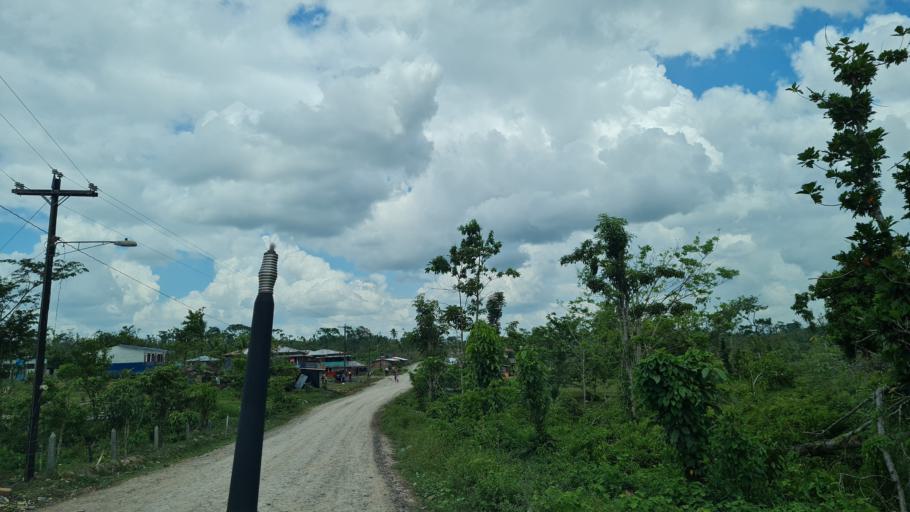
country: NI
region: Atlantico Norte (RAAN)
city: Siuna
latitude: 13.5901
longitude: -84.3406
